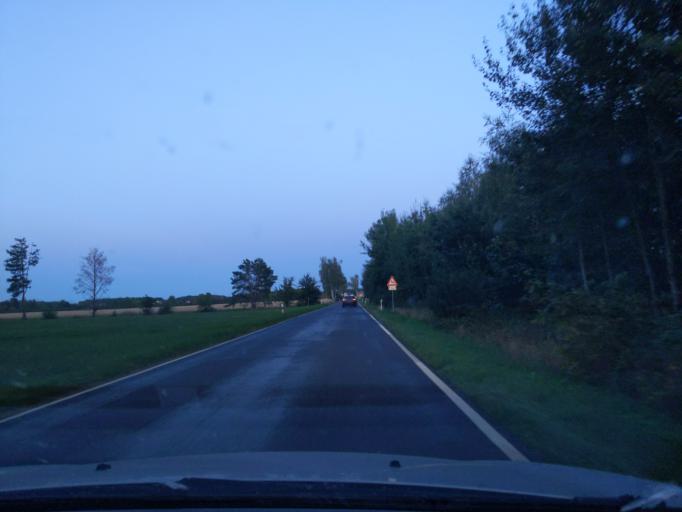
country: DE
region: Saxony
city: Konigswartha
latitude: 51.3446
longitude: 14.3621
